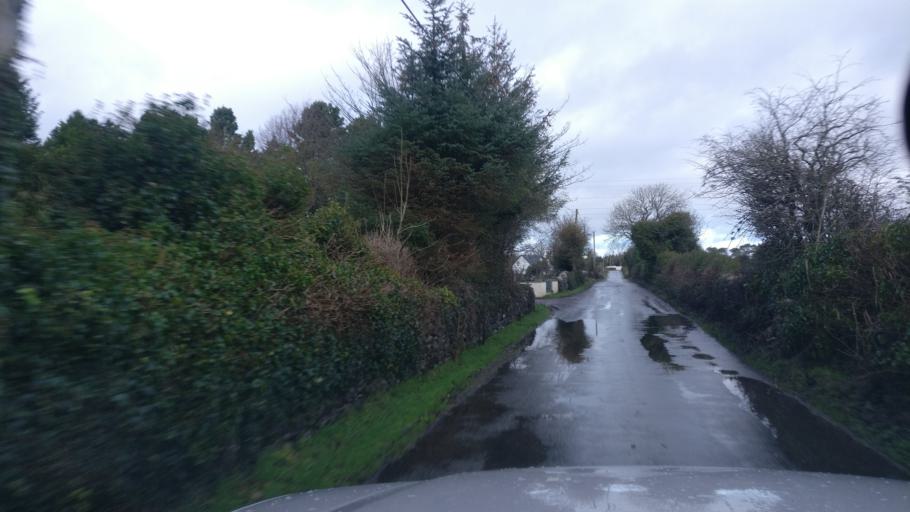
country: IE
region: Connaught
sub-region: County Galway
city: Loughrea
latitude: 53.2505
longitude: -8.6504
